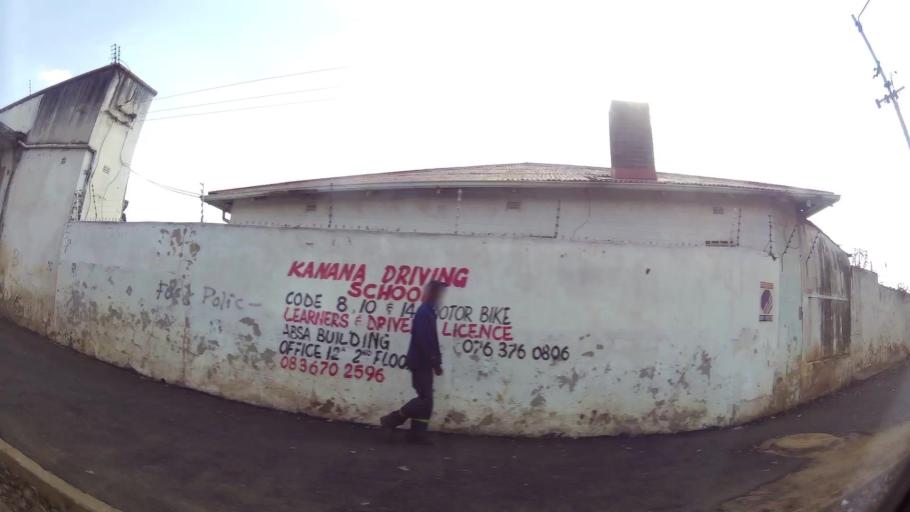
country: ZA
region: Gauteng
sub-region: Ekurhuleni Metropolitan Municipality
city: Germiston
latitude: -26.1849
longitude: 28.1728
